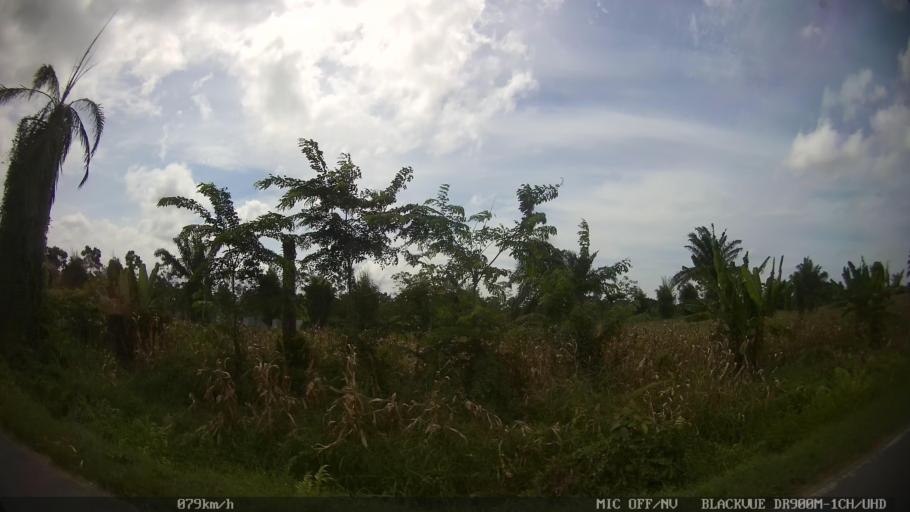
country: ID
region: North Sumatra
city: Percut
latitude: 3.6017
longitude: 98.8391
